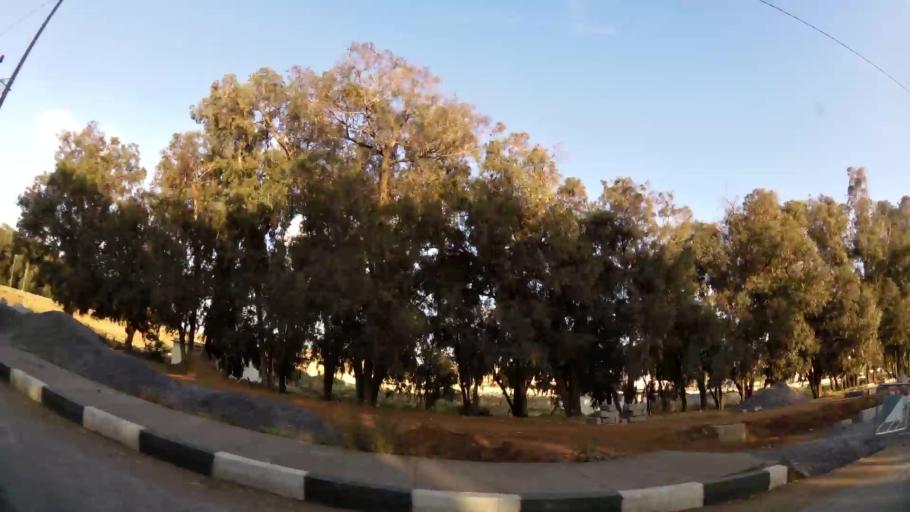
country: MA
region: Rabat-Sale-Zemmour-Zaer
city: Sale
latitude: 34.1293
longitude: -6.7339
